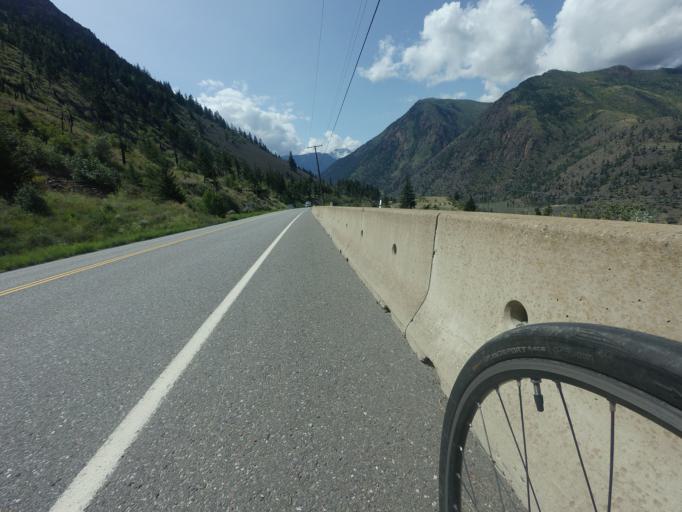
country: CA
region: British Columbia
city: Lillooet
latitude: 50.7543
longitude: -121.9230
